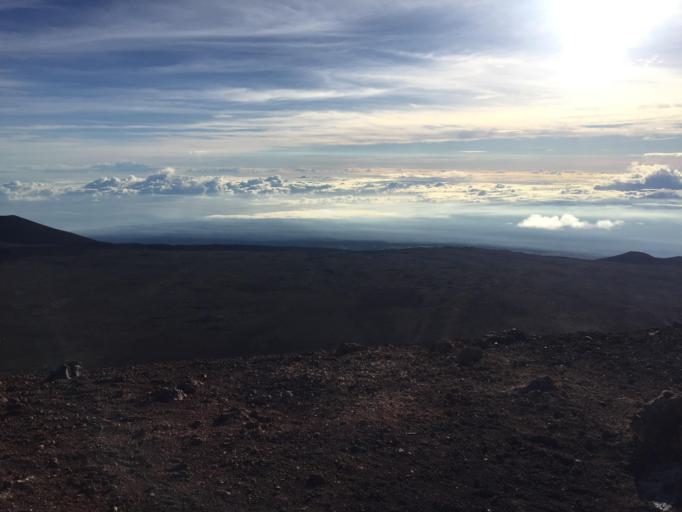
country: US
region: Hawaii
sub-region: Hawaii County
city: Honoka'a
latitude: 19.8207
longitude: -155.4681
